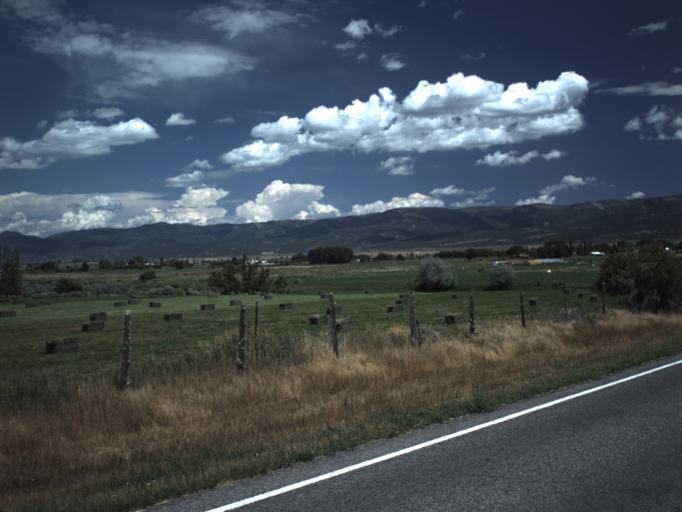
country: US
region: Utah
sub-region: Sanpete County
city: Mount Pleasant
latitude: 39.4818
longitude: -111.5098
